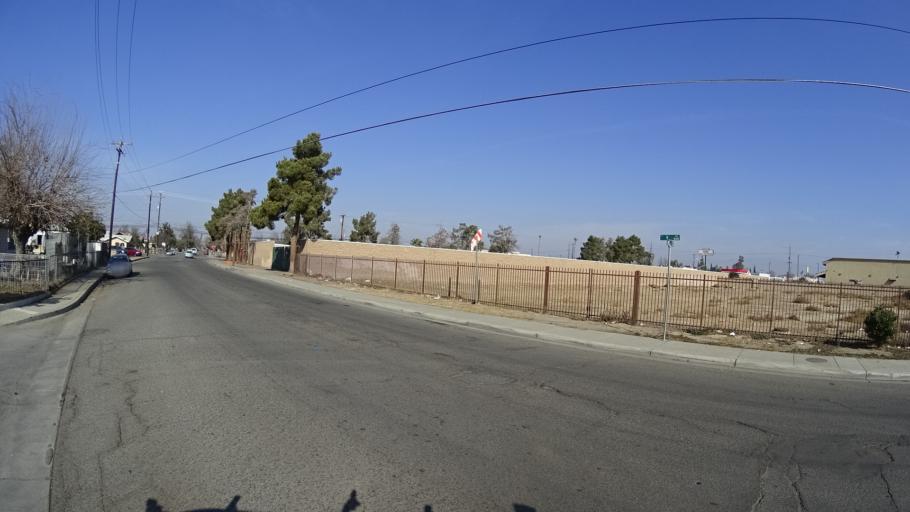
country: US
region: California
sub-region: Kern County
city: Bakersfield
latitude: 35.3598
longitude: -119.0052
